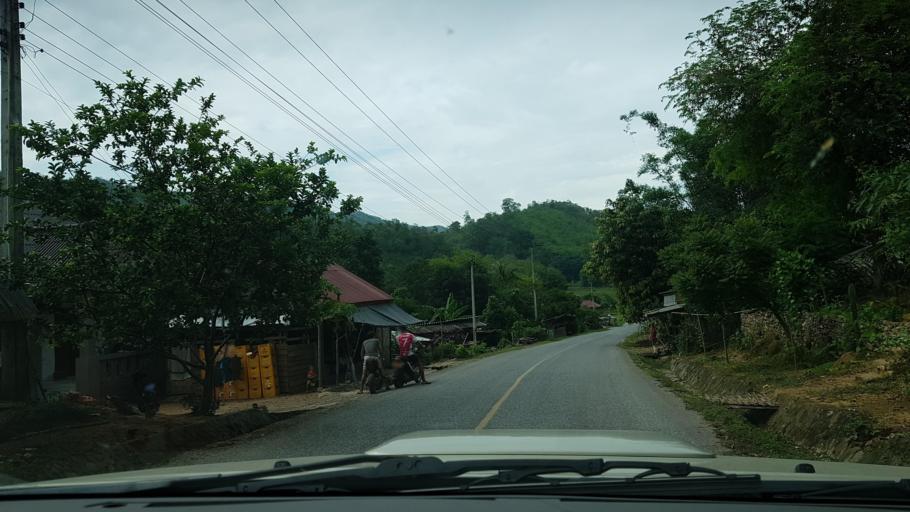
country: LA
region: Loungnamtha
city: Muang Nale
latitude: 20.3834
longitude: 101.7412
